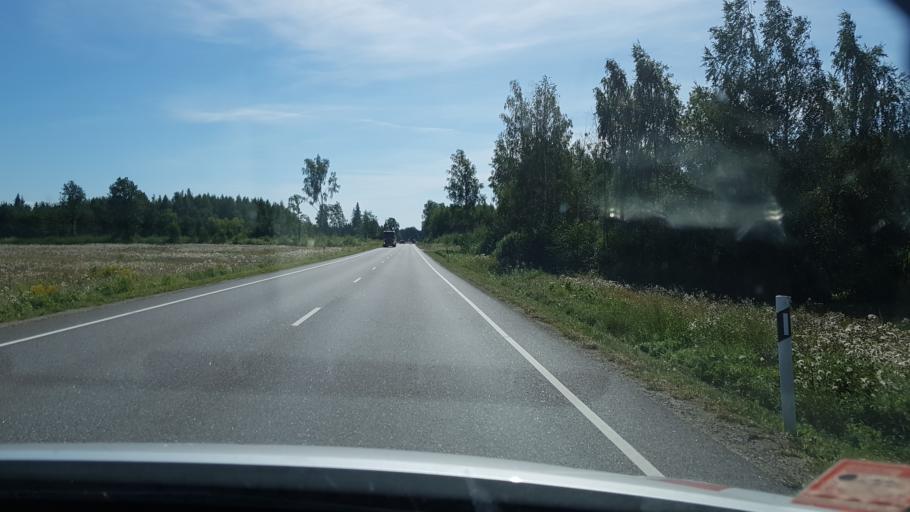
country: EE
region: Tartu
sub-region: Tartu linn
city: Tartu
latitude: 58.4409
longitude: 26.8207
